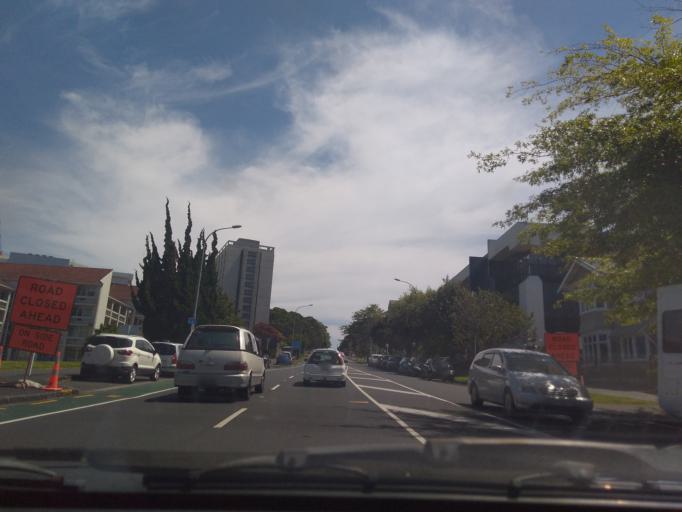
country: NZ
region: Auckland
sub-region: Auckland
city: Auckland
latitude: -36.8587
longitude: 174.7686
